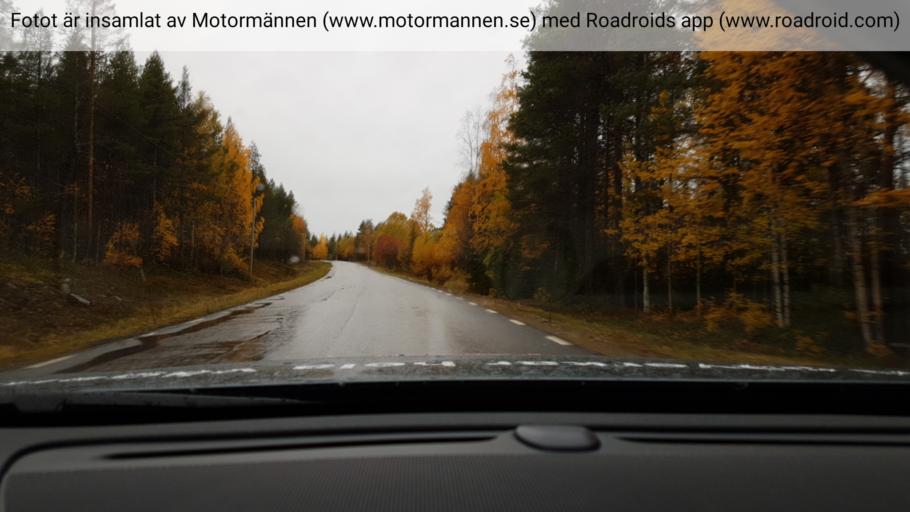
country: SE
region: Norrbotten
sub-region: Pajala Kommun
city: Pajala
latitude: 66.9218
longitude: 23.0179
